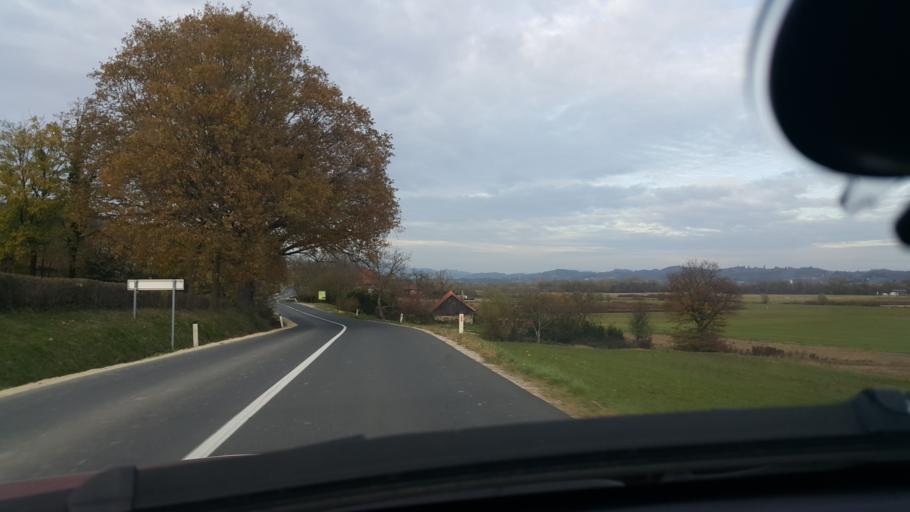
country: SI
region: Bistrica ob Sotli
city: Bistrica ob Sotli
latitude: 45.9700
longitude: 15.6948
